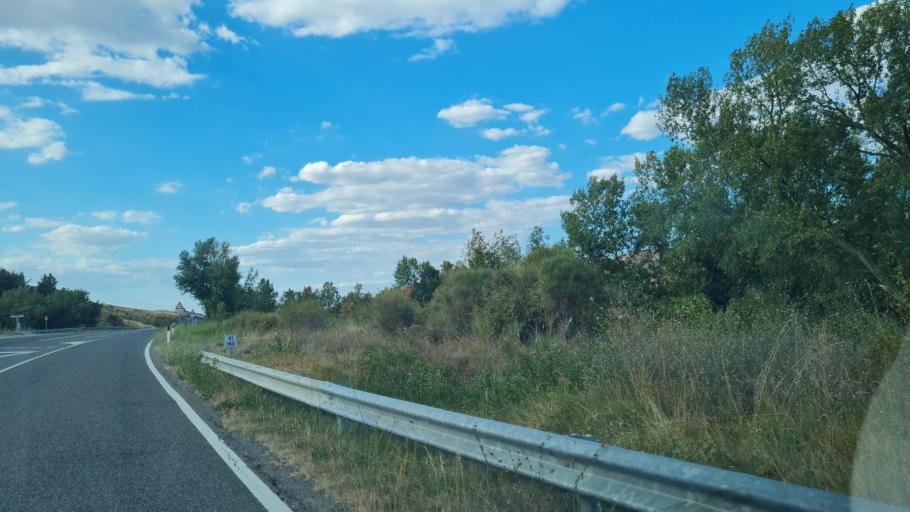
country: IT
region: Tuscany
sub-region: Provincia di Siena
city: Abbadia San Salvatore
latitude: 42.9493
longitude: 11.7081
